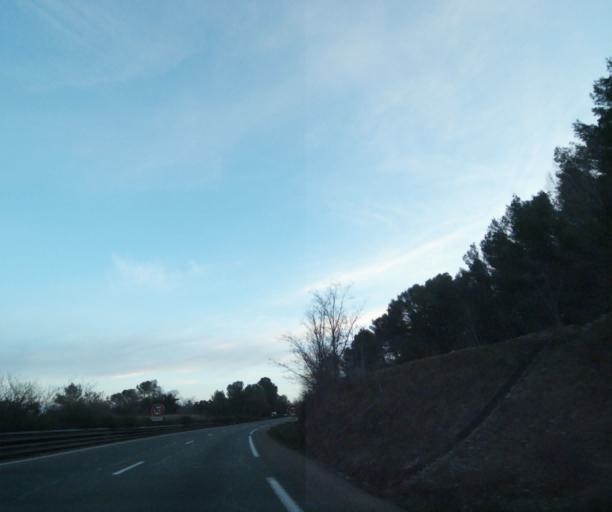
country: FR
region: Provence-Alpes-Cote d'Azur
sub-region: Departement du Var
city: Trans-en-Provence
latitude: 43.4920
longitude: 6.5058
